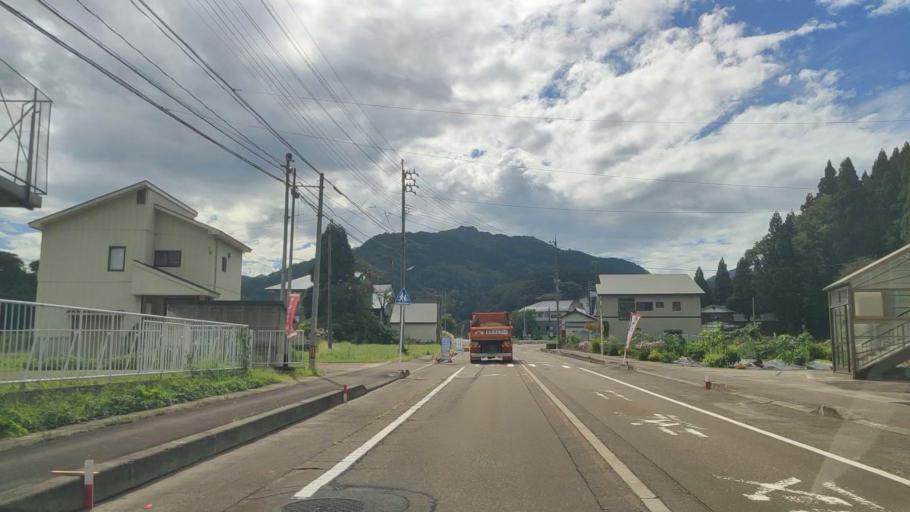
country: JP
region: Niigata
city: Arai
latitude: 36.9605
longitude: 138.2708
